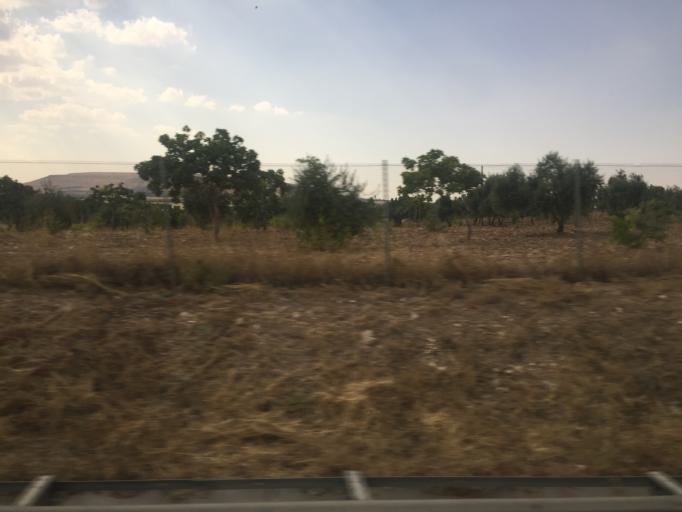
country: TR
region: Sanliurfa
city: Akziyaret
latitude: 37.2704
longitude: 38.7990
